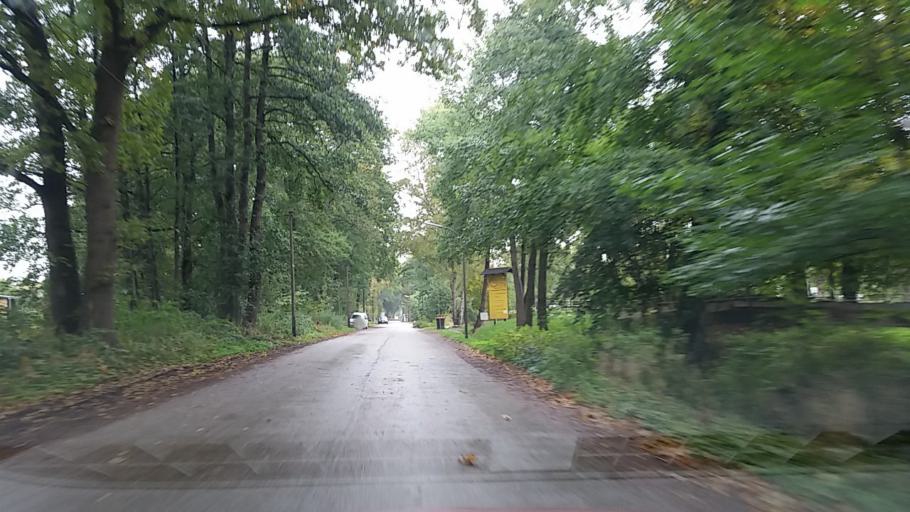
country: DE
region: Schleswig-Holstein
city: Oststeinbek
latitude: 53.5511
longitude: 10.1511
